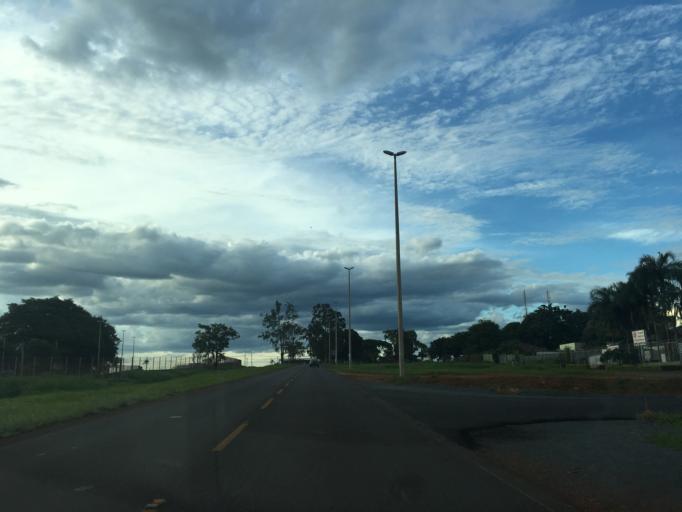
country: BR
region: Federal District
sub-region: Brasilia
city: Brasilia
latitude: -15.8356
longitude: -47.9402
